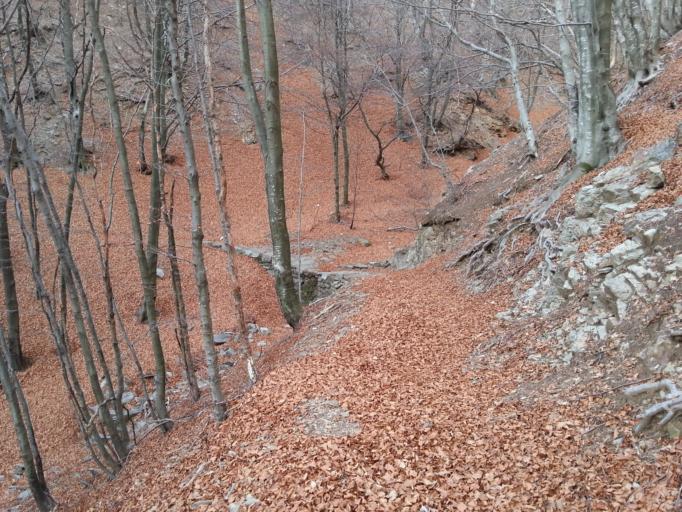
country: CH
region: Ticino
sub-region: Lugano District
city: Gravesano
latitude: 46.0555
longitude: 8.8672
